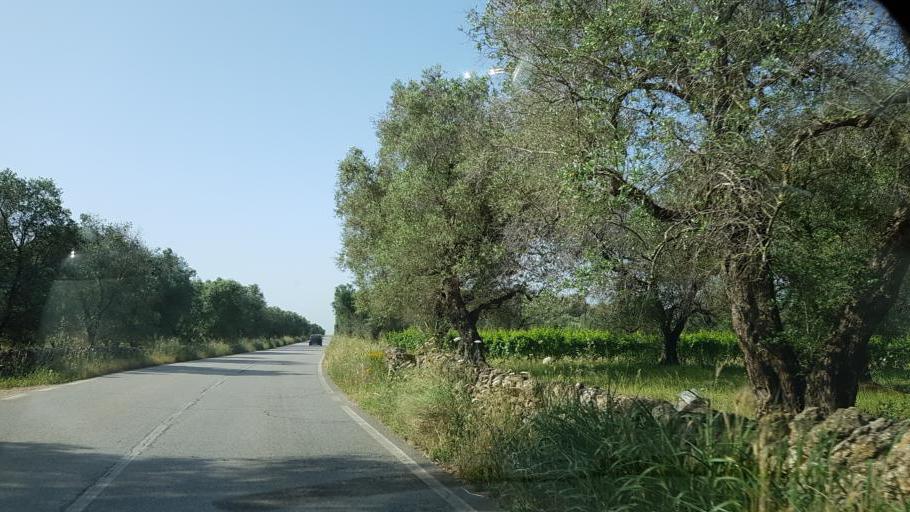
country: IT
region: Apulia
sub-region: Provincia di Brindisi
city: Mesagne
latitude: 40.5166
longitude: 17.8258
